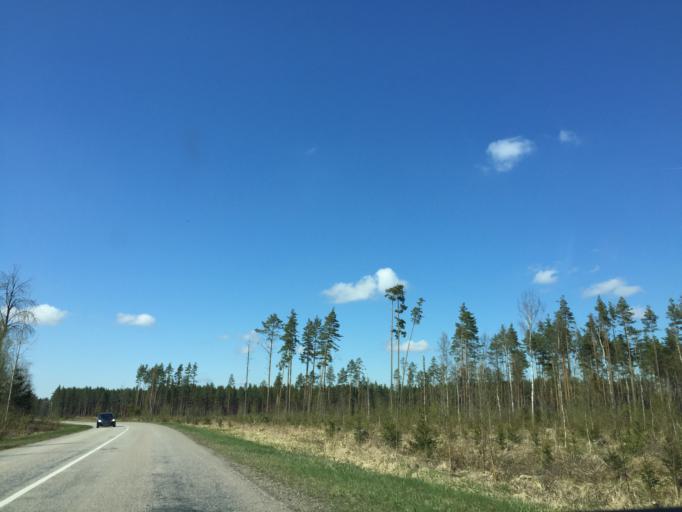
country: LV
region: Strenci
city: Seda
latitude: 57.5839
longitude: 25.7519
